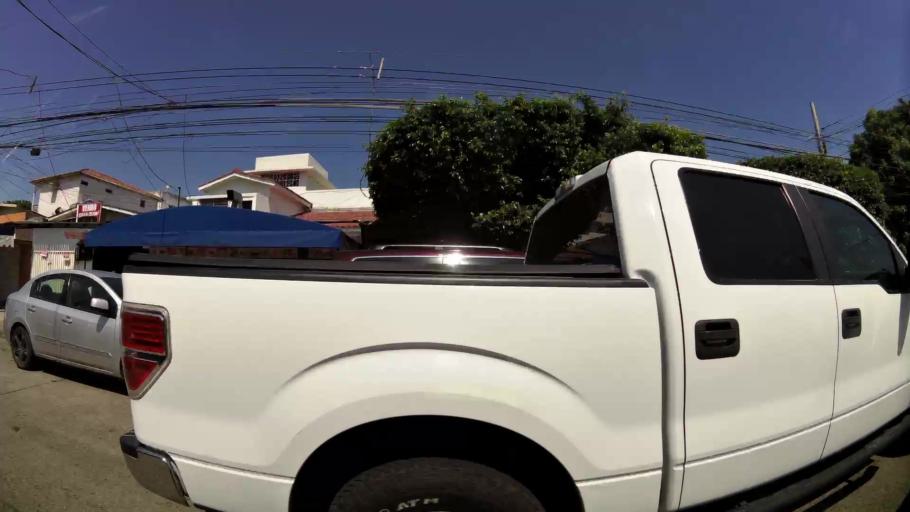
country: EC
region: Guayas
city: Guayaquil
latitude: -2.1661
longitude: -79.9120
